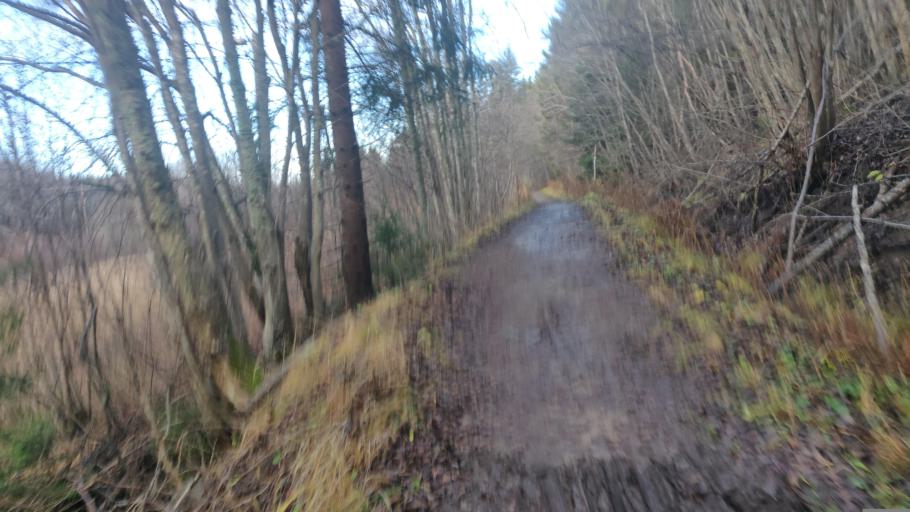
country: SE
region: Vaesternorrland
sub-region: Sundsvalls Kommun
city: Nolby
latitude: 62.3024
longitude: 17.3561
